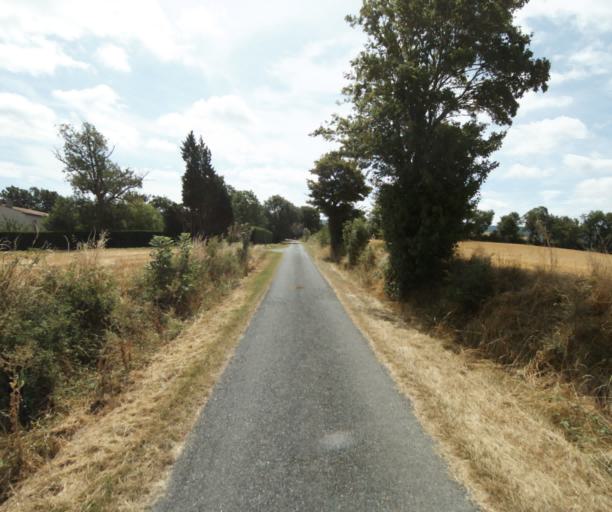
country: FR
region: Midi-Pyrenees
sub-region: Departement du Tarn
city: Dourgne
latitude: 43.4909
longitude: 2.1050
